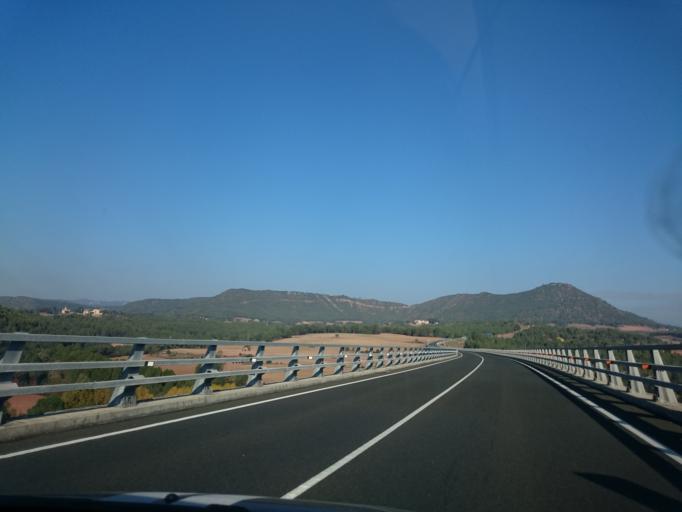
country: ES
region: Catalonia
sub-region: Provincia de Barcelona
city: Sant Joan de Vilatorrada
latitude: 41.7167
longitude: 1.7845
